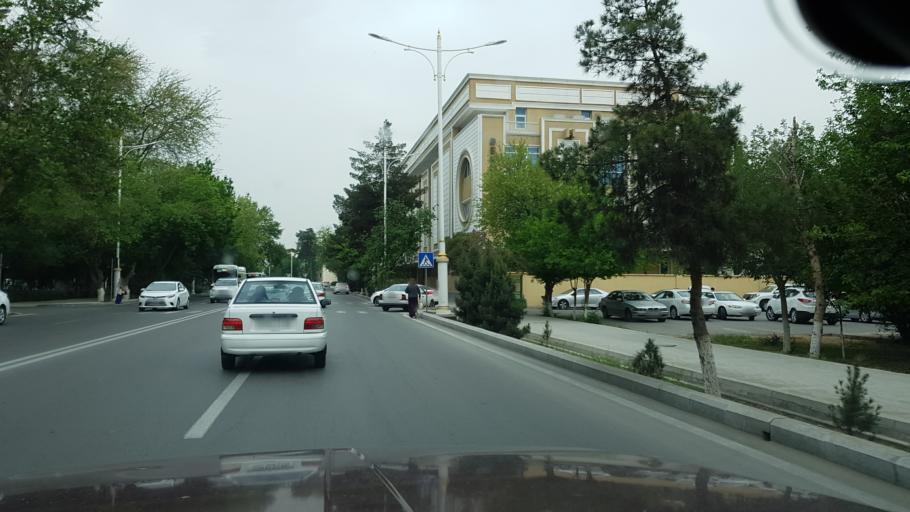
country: TM
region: Ahal
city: Ashgabat
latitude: 37.9349
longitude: 58.3919
